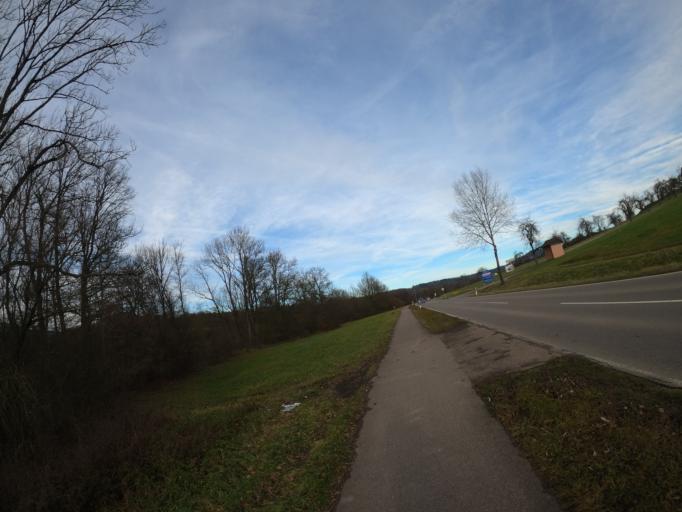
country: DE
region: Baden-Wuerttemberg
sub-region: Regierungsbezirk Stuttgart
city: Ottenbach
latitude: 48.7220
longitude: 9.7383
